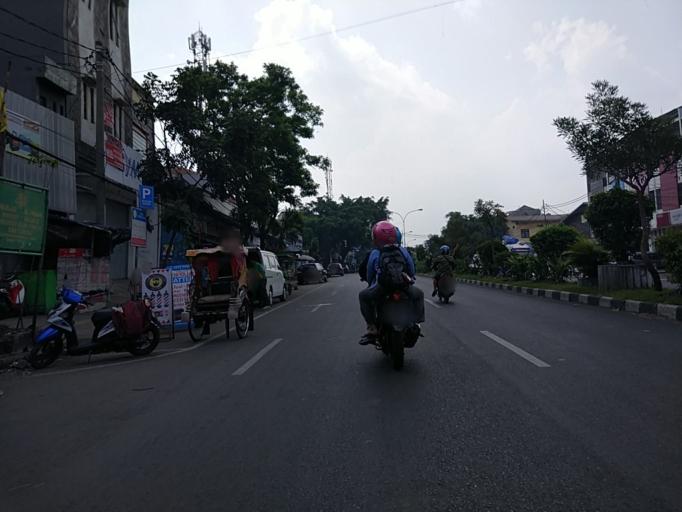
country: ID
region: West Java
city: Bandung
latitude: -6.9243
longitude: 107.5856
